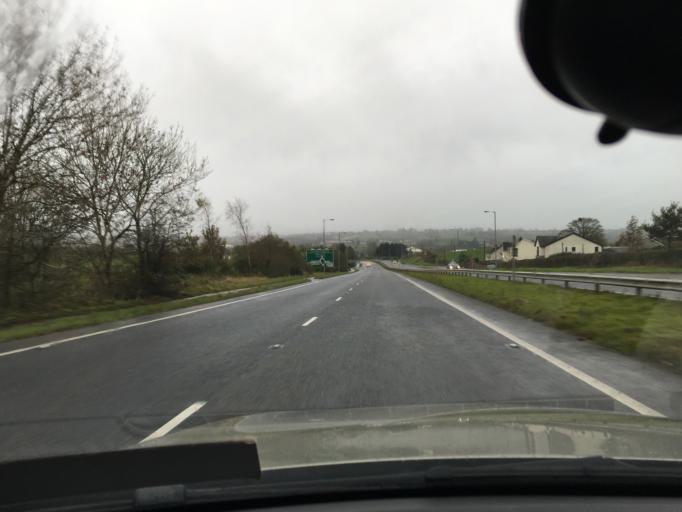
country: GB
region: Northern Ireland
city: Carnmoney
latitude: 54.7090
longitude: -5.9679
